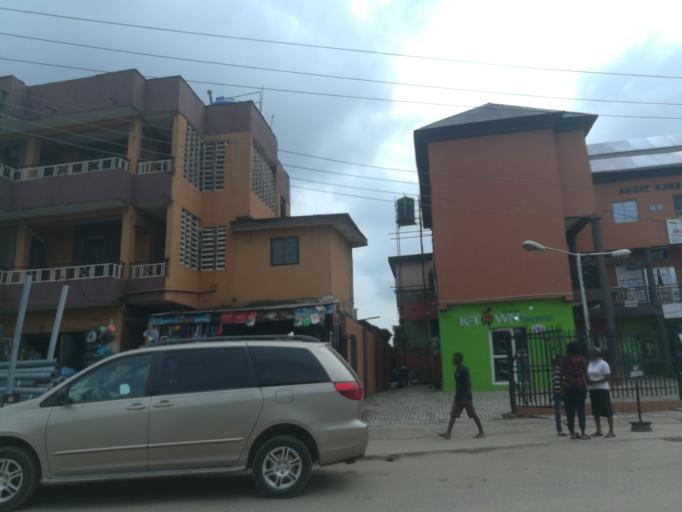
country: NG
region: Lagos
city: Somolu
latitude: 6.5477
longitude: 3.3944
